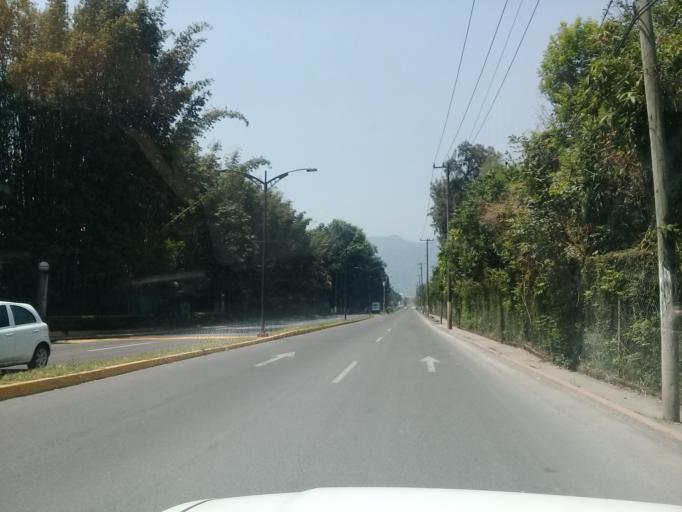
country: MX
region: Veracruz
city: Ixtac Zoquitlan
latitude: 18.8617
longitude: -97.0432
